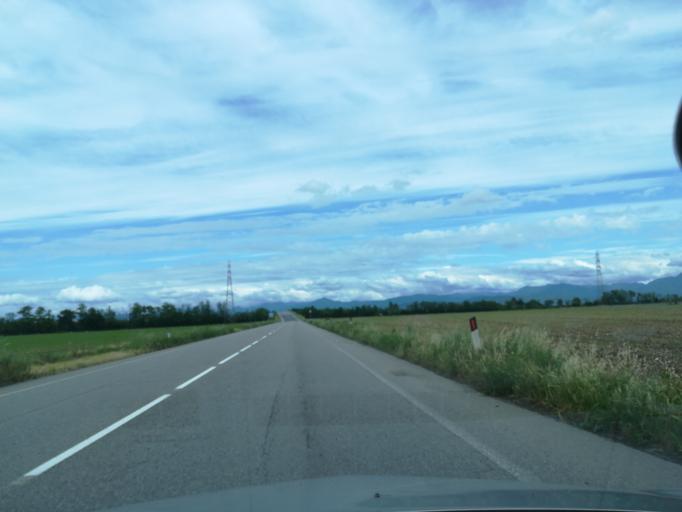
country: IT
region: Lombardy
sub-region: Provincia di Bergamo
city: Calcio
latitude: 45.5278
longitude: 9.8335
